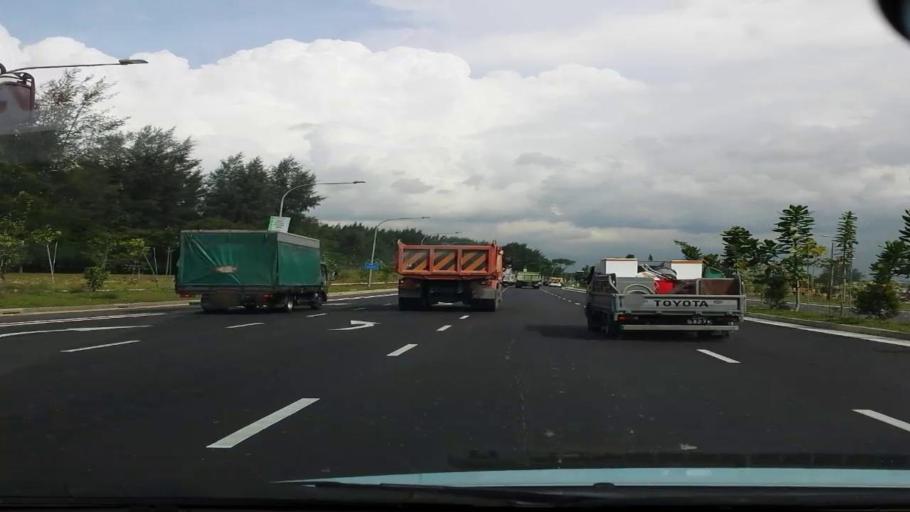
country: SG
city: Singapore
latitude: 1.3185
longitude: 103.9840
